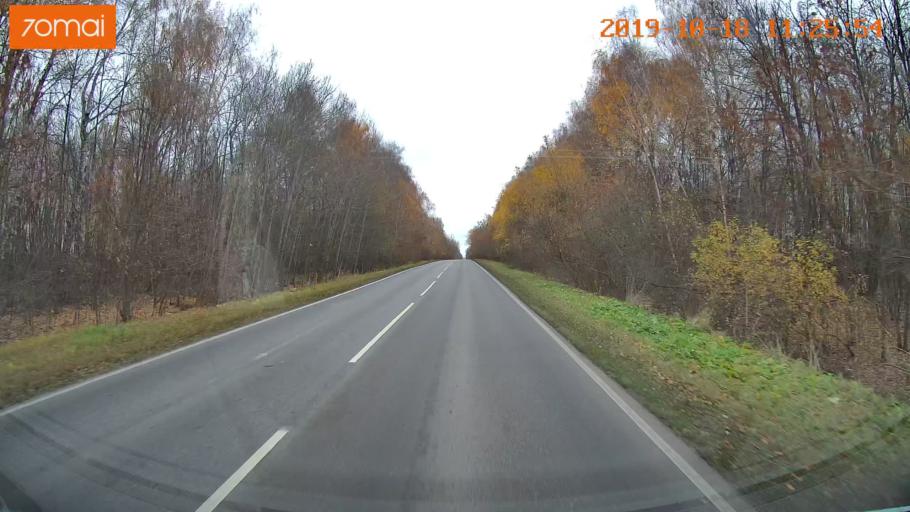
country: RU
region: Tula
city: Kimovsk
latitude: 54.1290
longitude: 38.6271
